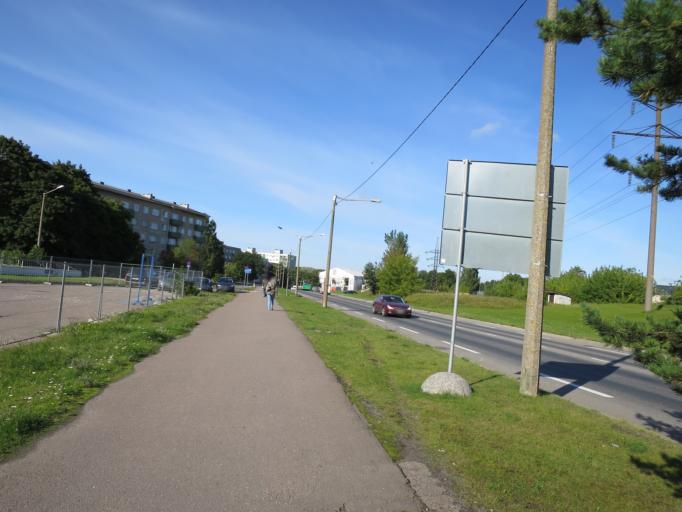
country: EE
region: Harju
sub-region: Tallinna linn
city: Tallinn
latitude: 59.4000
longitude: 24.7058
